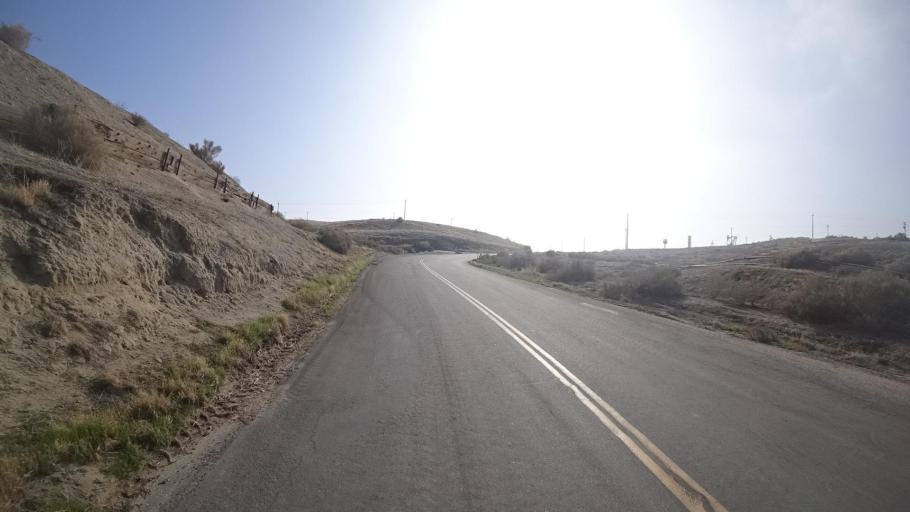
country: US
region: California
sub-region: Kern County
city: Ford City
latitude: 35.1666
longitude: -119.4209
